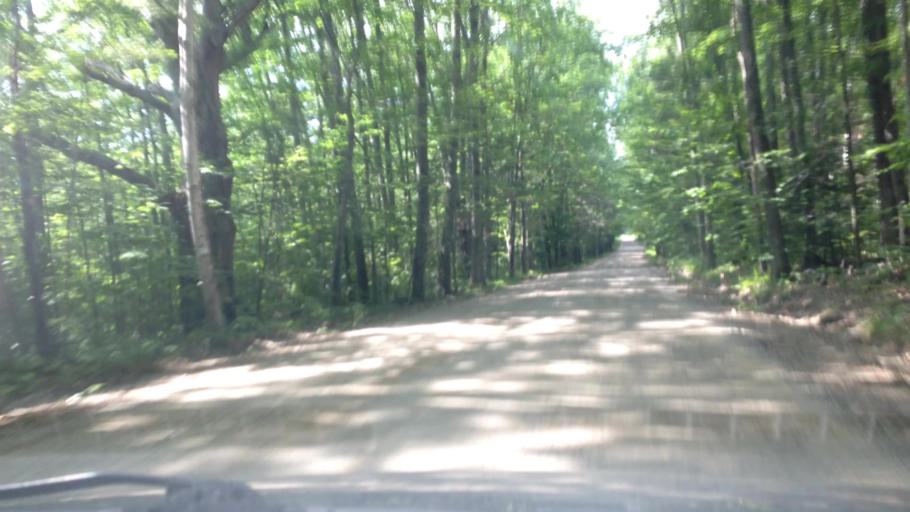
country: US
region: New Hampshire
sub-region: Cheshire County
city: Marlborough
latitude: 42.8861
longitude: -72.1903
